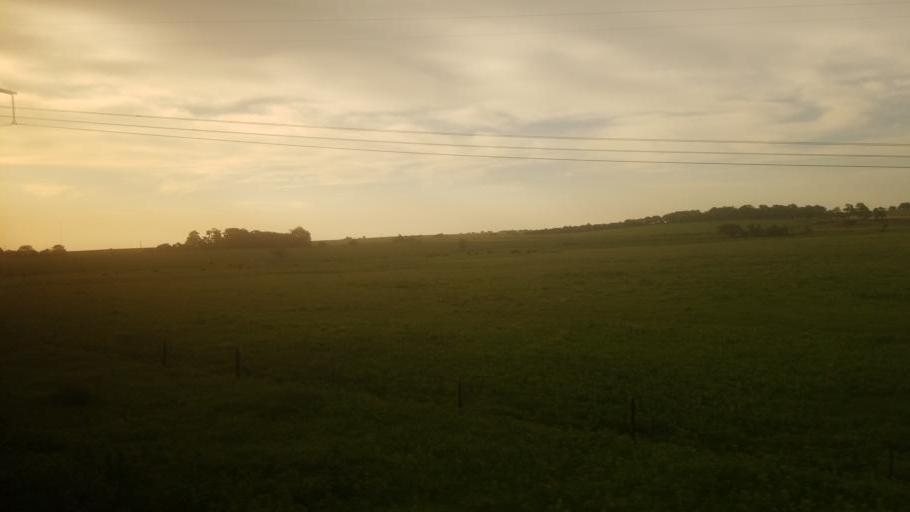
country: US
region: Kansas
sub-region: Lyon County
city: Emporia
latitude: 38.4907
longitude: -96.0299
